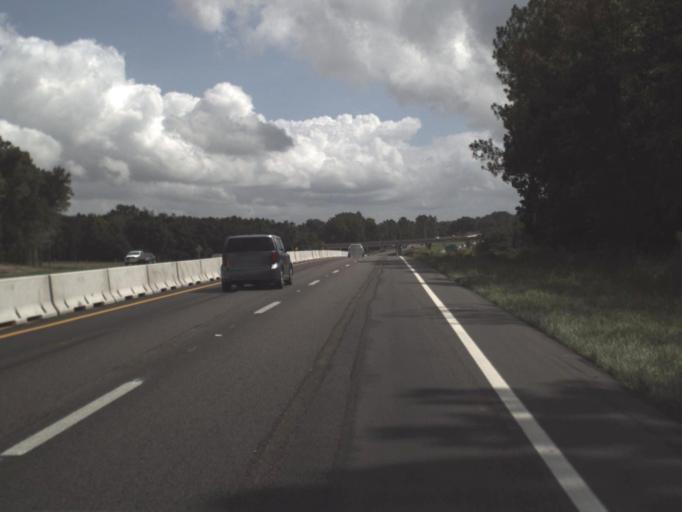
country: US
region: Florida
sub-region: Pasco County
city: San Antonio
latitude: 28.4162
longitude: -82.2939
